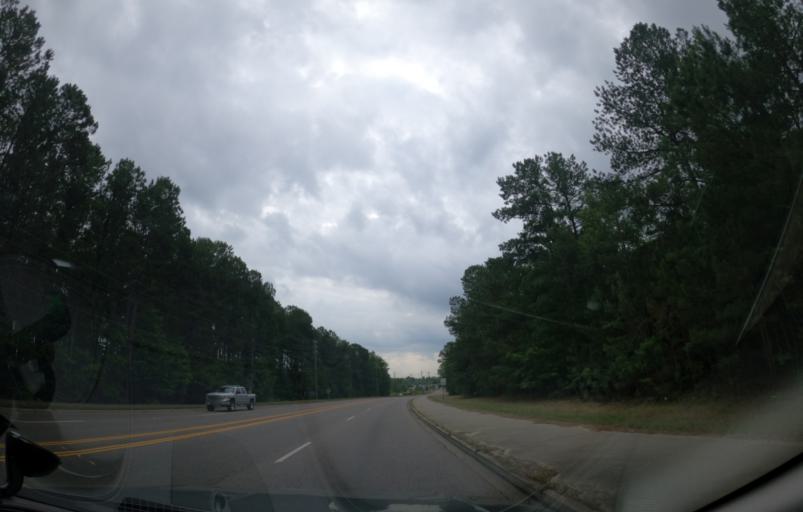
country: US
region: South Carolina
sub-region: Aiken County
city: Aiken
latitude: 33.5787
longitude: -81.7085
